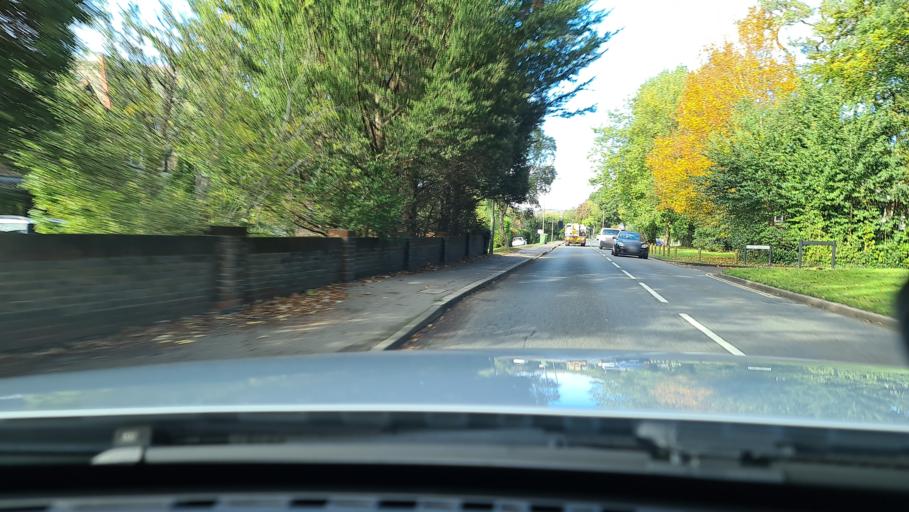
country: GB
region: England
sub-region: Surrey
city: Byfleet
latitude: 51.3446
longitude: -0.4633
